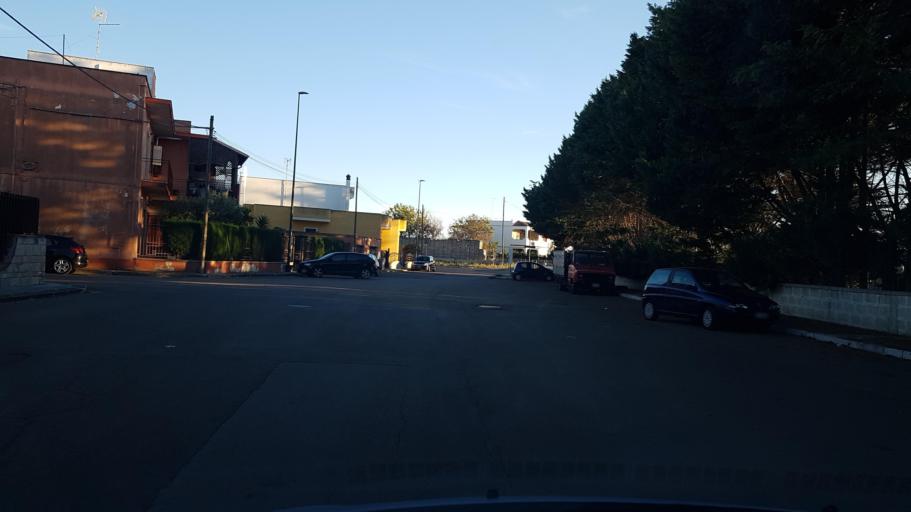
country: IT
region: Apulia
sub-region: Provincia di Lecce
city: Guagnano
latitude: 40.3983
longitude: 17.9479
